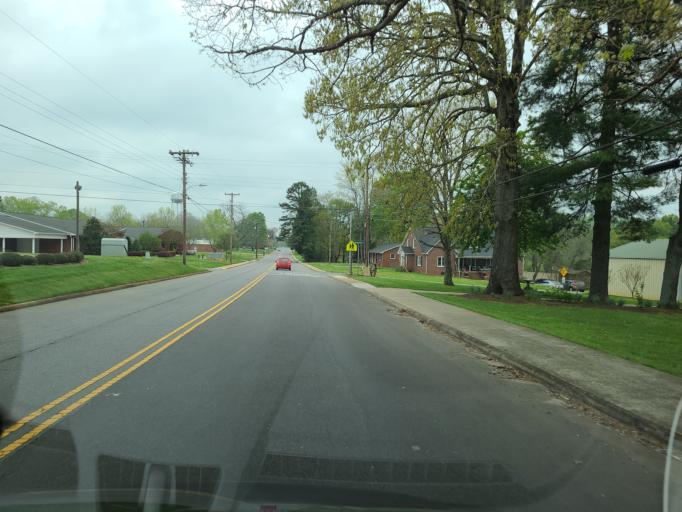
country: US
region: North Carolina
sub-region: Gaston County
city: Cherryville
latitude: 35.4271
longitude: -81.4962
